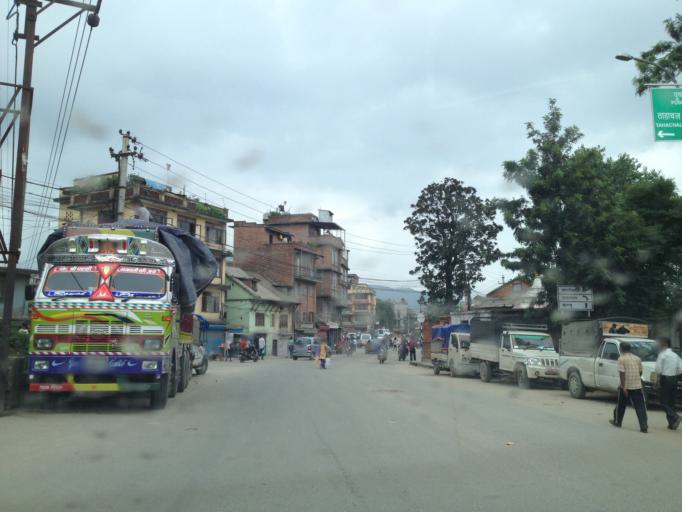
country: NP
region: Central Region
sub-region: Bagmati Zone
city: Kathmandu
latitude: 27.7004
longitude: 85.3024
